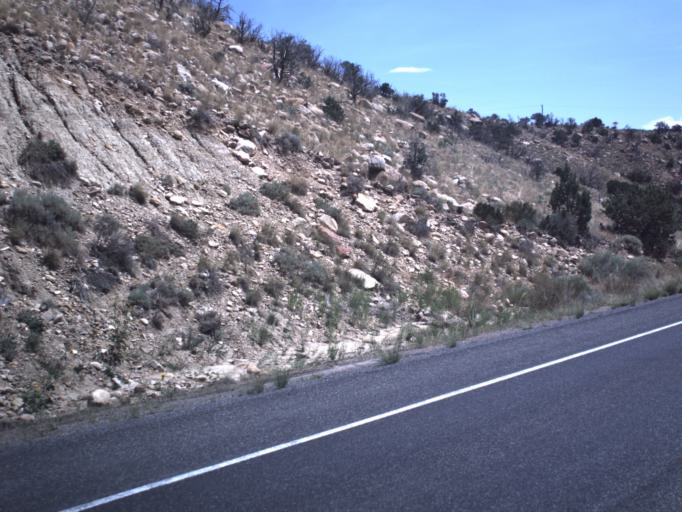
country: US
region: Utah
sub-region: Emery County
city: Huntington
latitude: 39.3711
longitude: -111.0611
